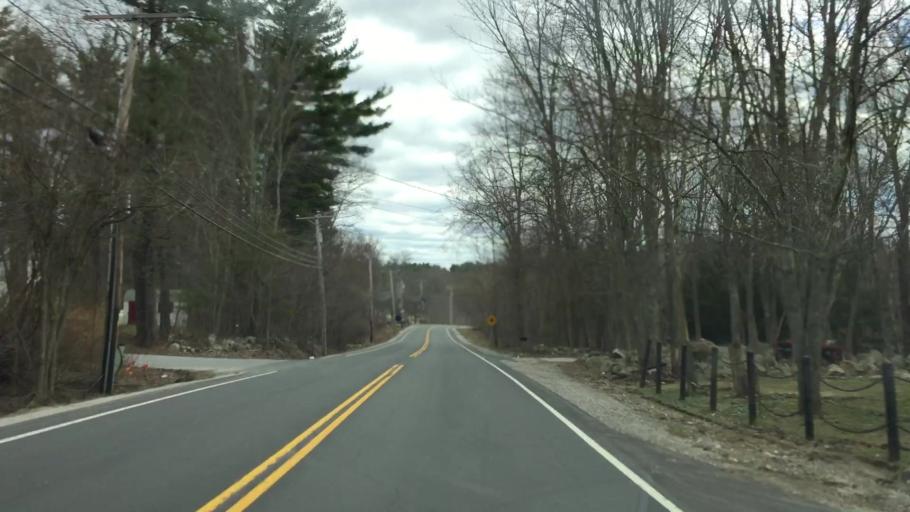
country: US
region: New Hampshire
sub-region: Rockingham County
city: Windham
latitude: 42.8093
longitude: -71.3550
